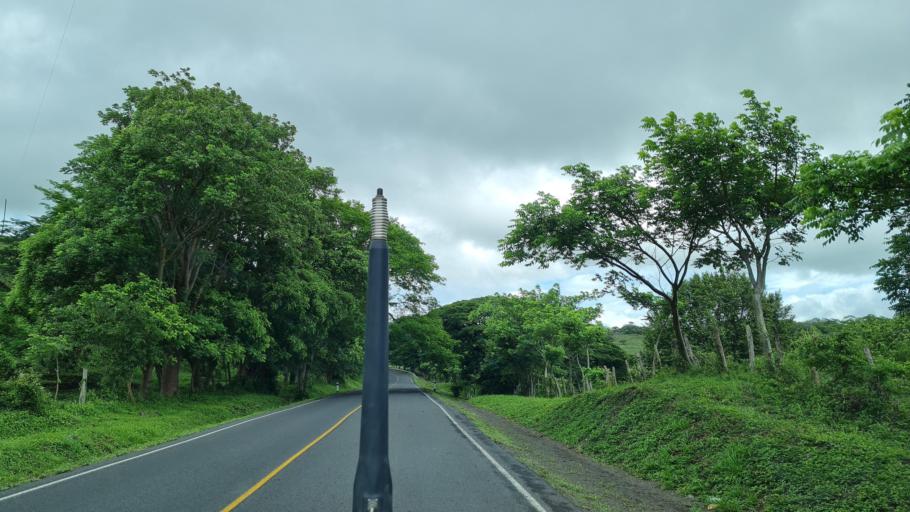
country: NI
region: Matagalpa
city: Terrabona
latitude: 12.5957
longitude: -85.9269
